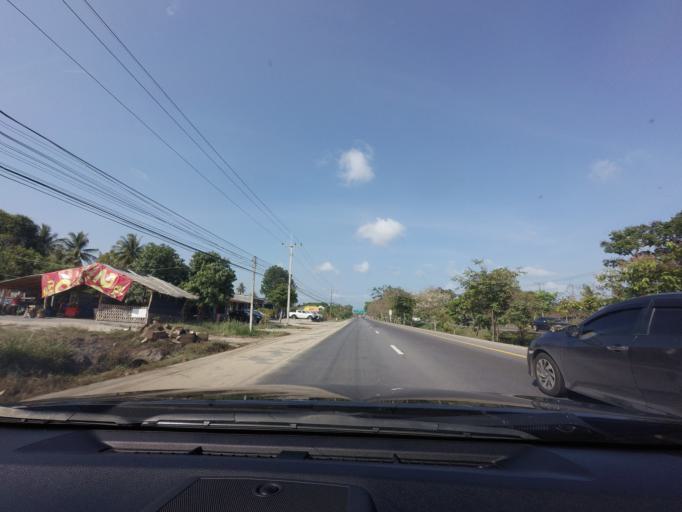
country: TH
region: Prachuap Khiri Khan
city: Prachuap Khiri Khan
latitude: 11.7445
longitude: 99.7536
